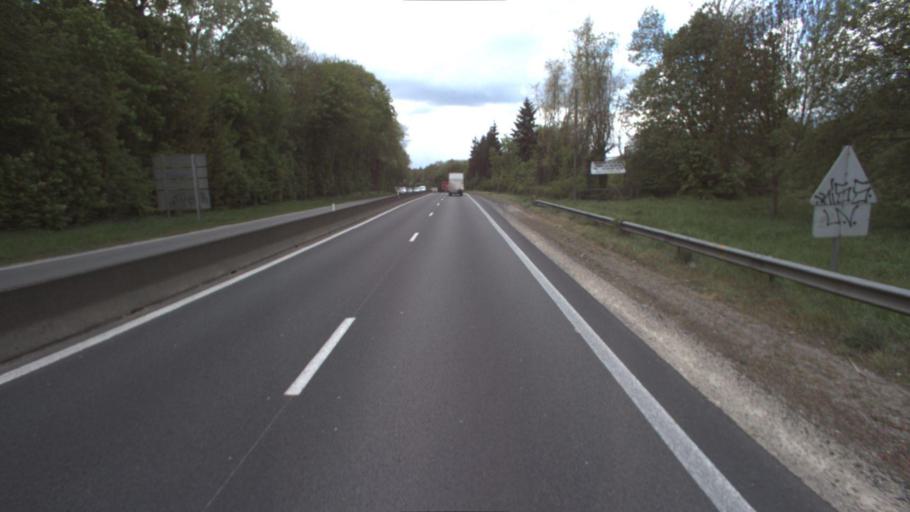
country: FR
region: Ile-de-France
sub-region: Departement de Seine-et-Marne
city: Tournan-en-Brie
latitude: 48.7363
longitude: 2.7680
